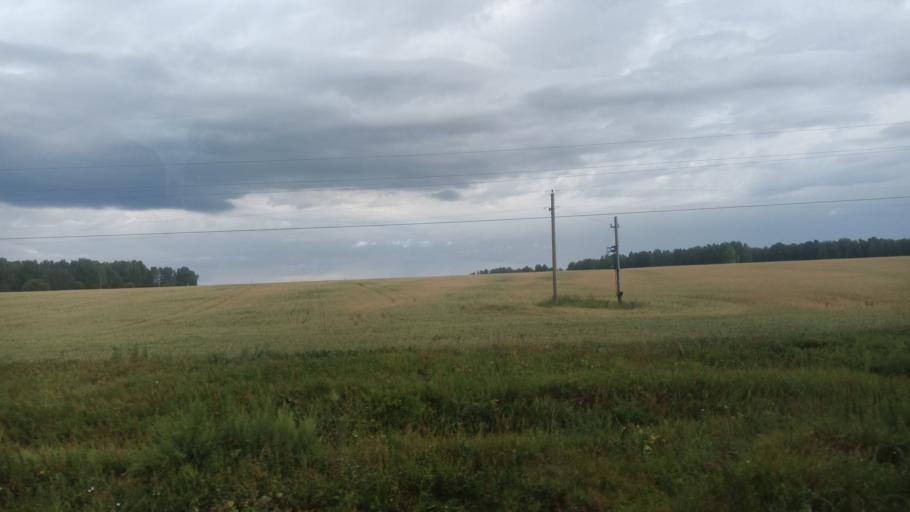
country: RU
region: Altai Krai
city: Nalobikha
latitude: 53.2330
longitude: 84.5095
